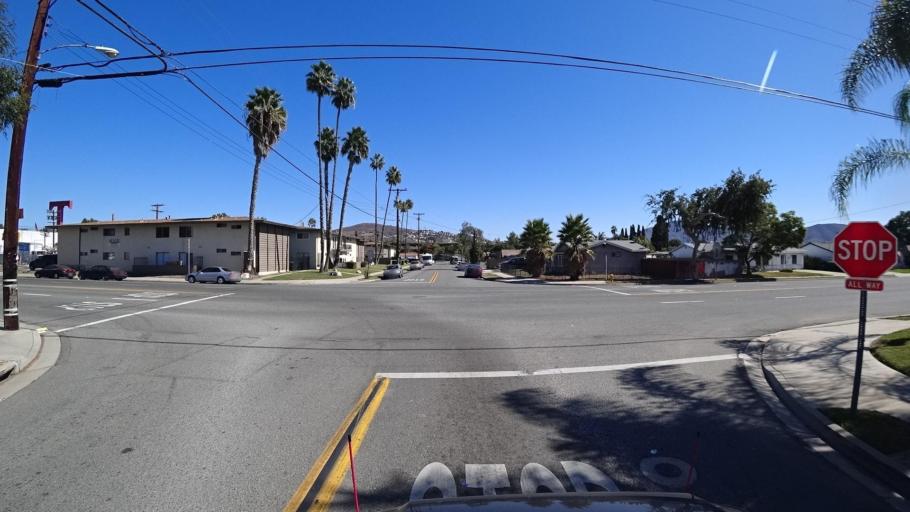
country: US
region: California
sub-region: San Diego County
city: La Presa
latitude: 32.7122
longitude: -117.0166
